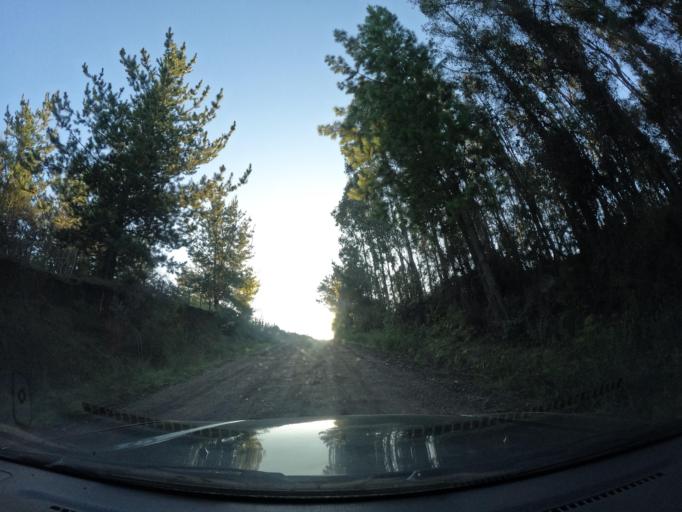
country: CL
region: Biobio
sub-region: Provincia de Concepcion
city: Chiguayante
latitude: -37.0143
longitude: -72.8422
